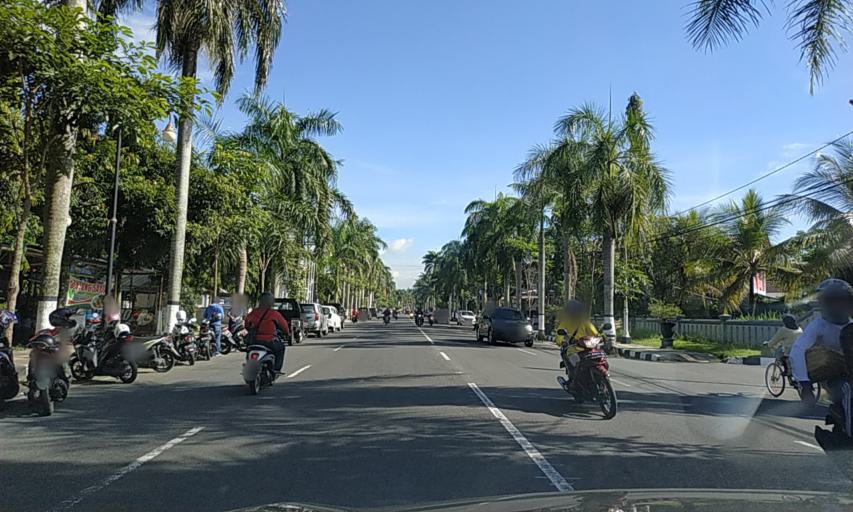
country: ID
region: Central Java
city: Muntilan
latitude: -7.5972
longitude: 110.2223
